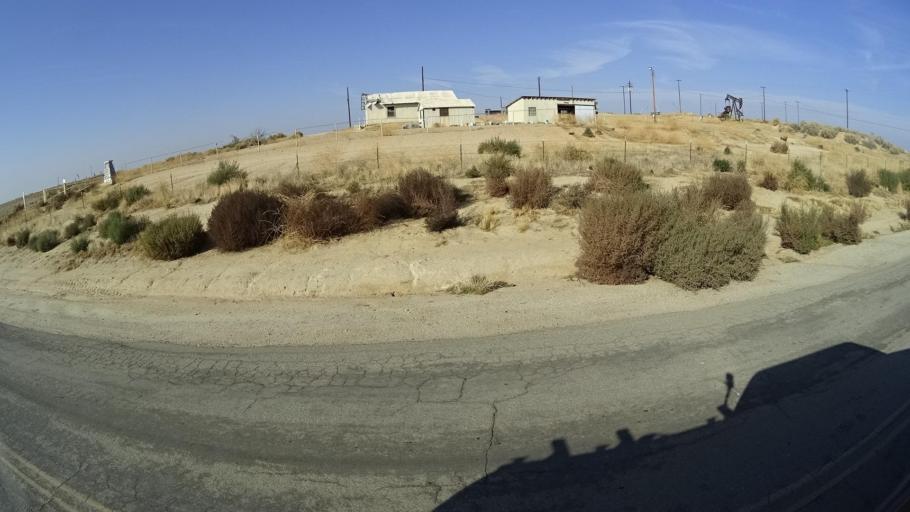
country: US
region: California
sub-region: Kern County
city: Oildale
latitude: 35.4925
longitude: -119.0409
